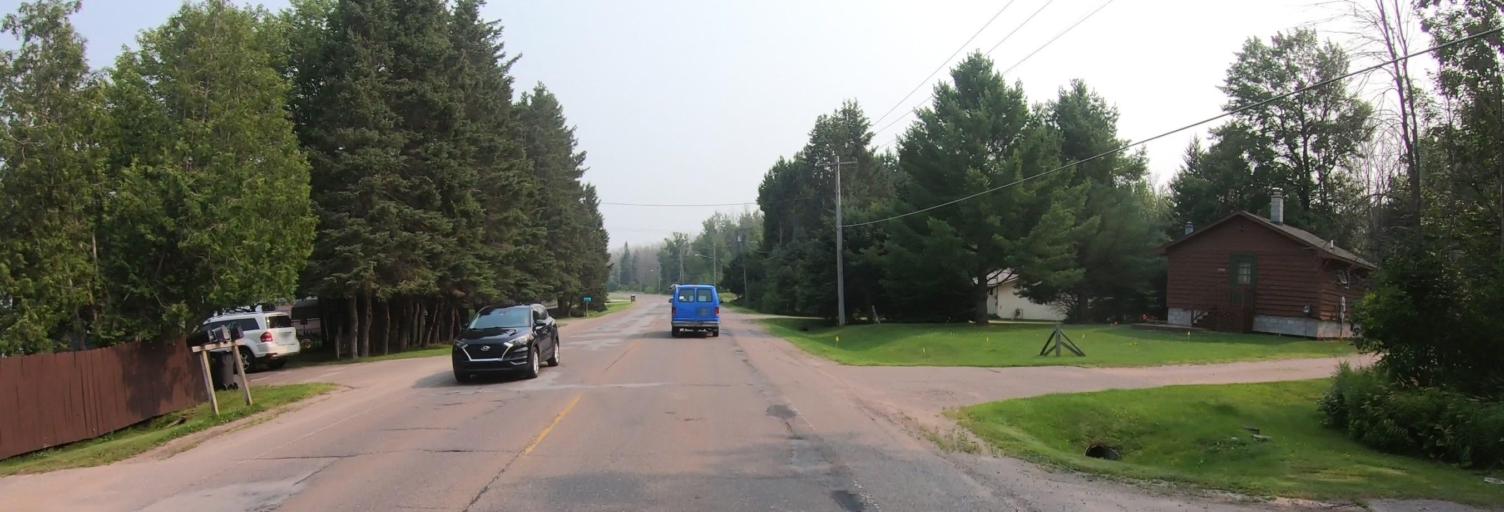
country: US
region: Michigan
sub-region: Chippewa County
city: Sault Ste. Marie
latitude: 46.4752
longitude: -84.3037
